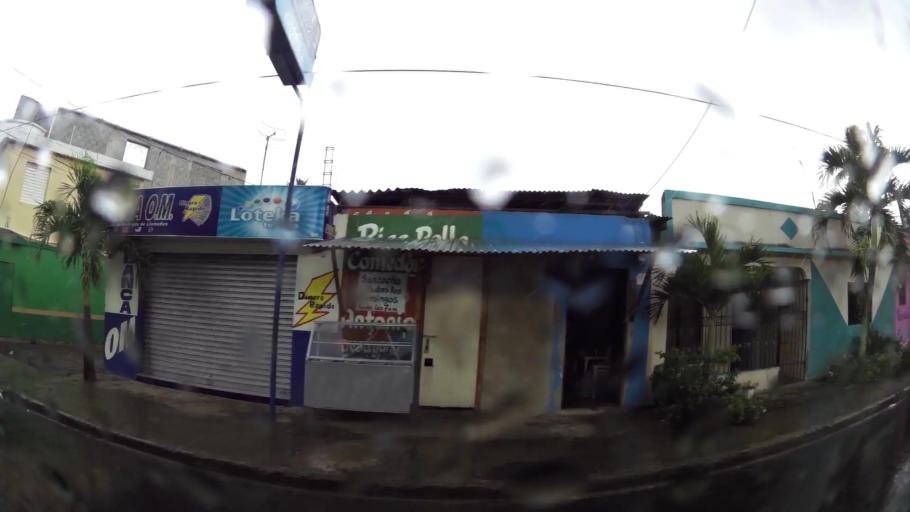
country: DO
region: Monsenor Nouel
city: Bonao
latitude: 18.9471
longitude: -70.4066
